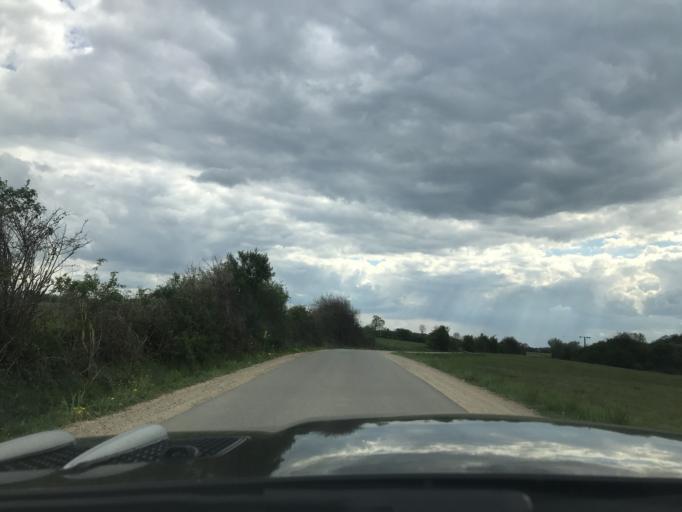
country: DE
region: Schleswig-Holstein
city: Gross Gronau
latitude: 53.7846
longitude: 10.7844
